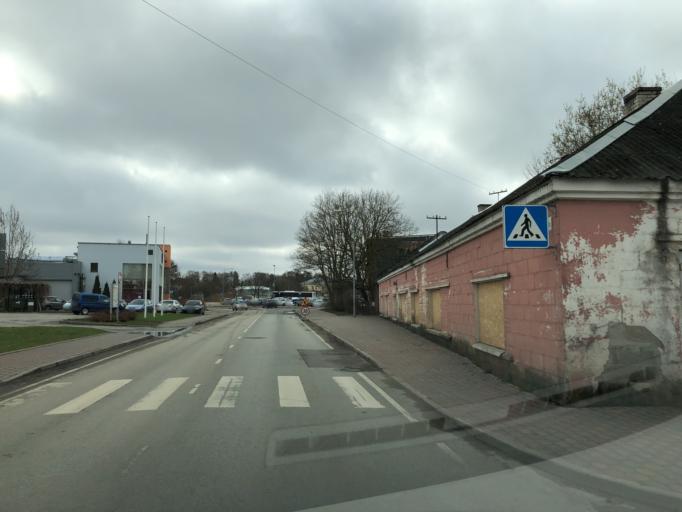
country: EE
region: Laeaene-Virumaa
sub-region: Rakvere linn
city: Rakvere
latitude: 59.3491
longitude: 26.3572
